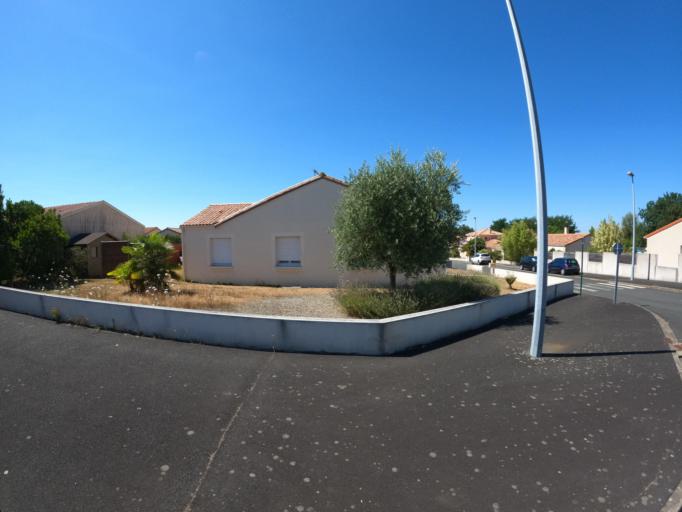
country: FR
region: Pays de la Loire
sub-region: Departement de Maine-et-Loire
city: Saint-Christophe-du-Bois
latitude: 47.0318
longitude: -0.9512
